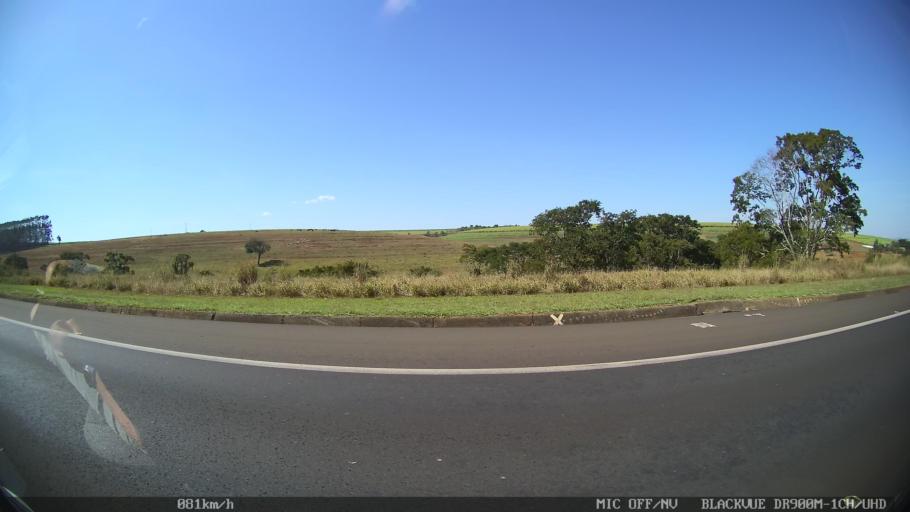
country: BR
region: Sao Paulo
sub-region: Franca
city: Franca
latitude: -20.6983
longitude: -47.5003
